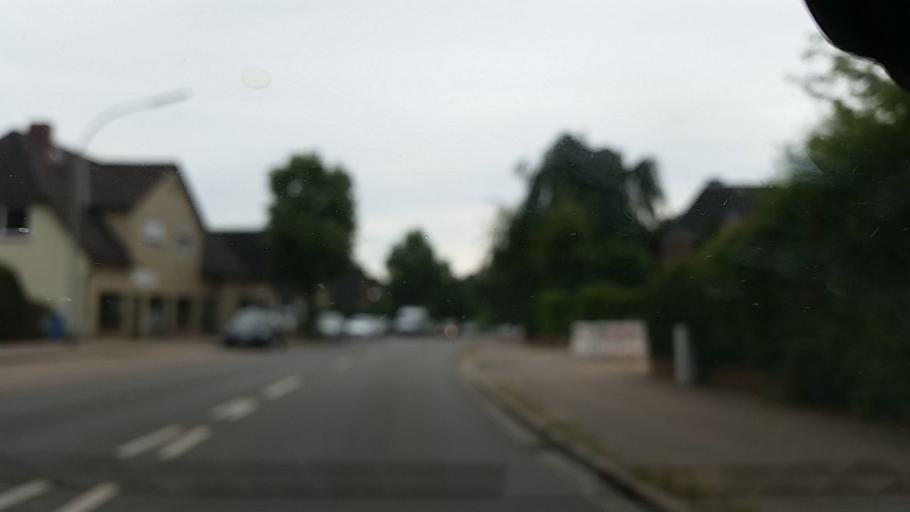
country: DE
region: Schleswig-Holstein
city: Reinbek
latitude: 53.5238
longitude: 10.2584
